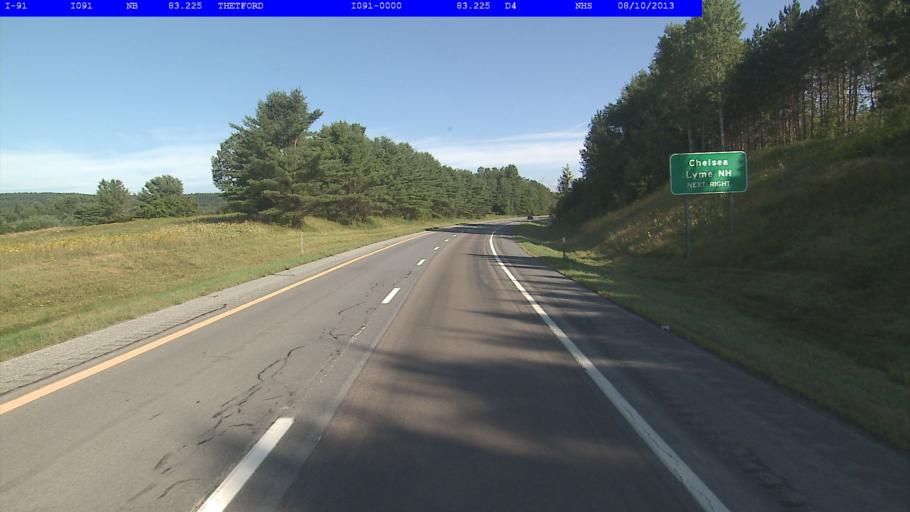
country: US
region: New Hampshire
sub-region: Grafton County
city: Lyme
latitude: 43.7985
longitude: -72.2183
